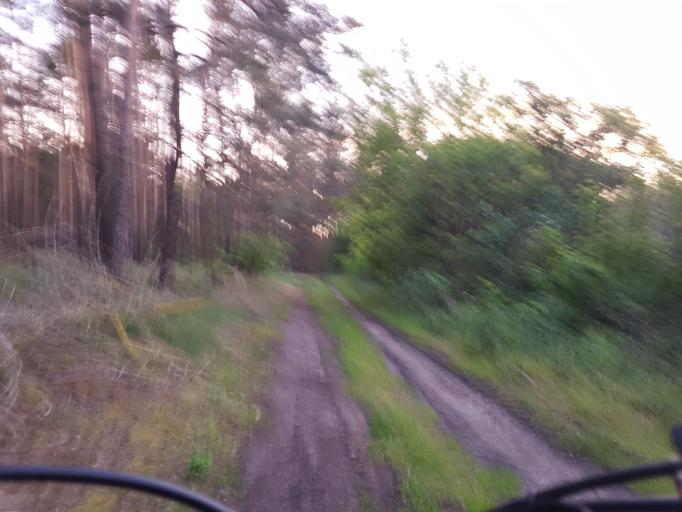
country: DE
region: Brandenburg
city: Schilda
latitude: 51.5709
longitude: 13.3680
